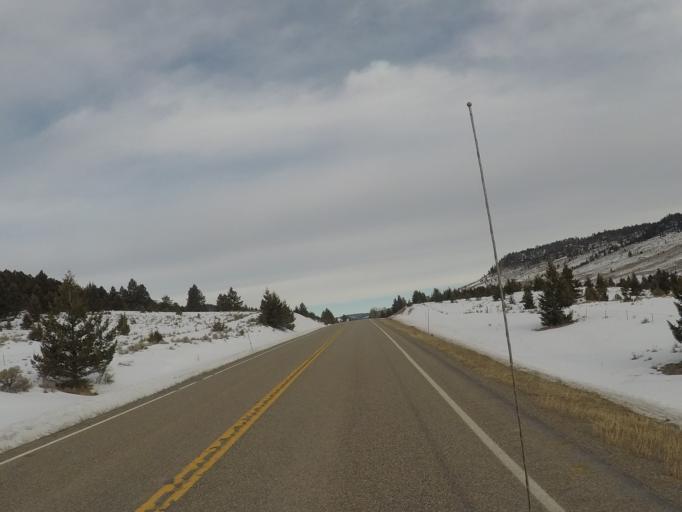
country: US
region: Montana
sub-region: Meagher County
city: White Sulphur Springs
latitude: 46.6347
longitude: -110.8546
